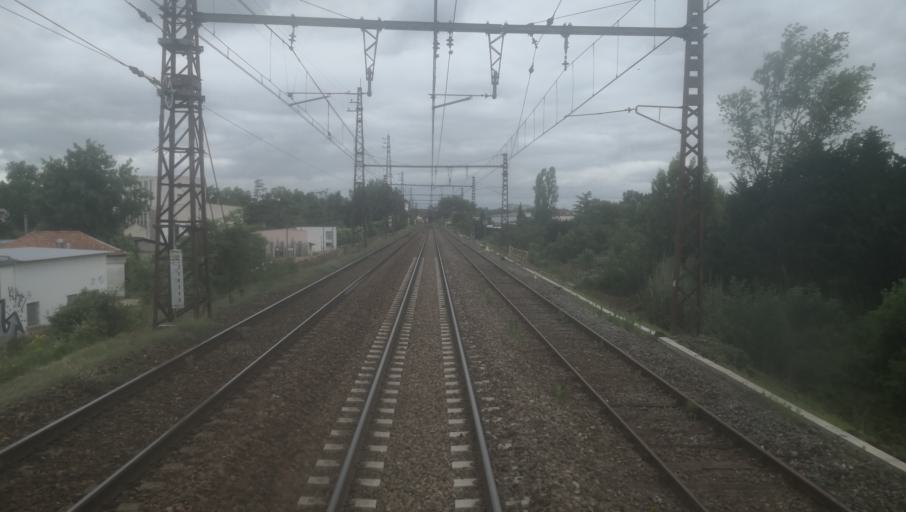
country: FR
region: Midi-Pyrenees
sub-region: Departement du Tarn-et-Garonne
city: Montauban
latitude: 44.0015
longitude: 1.3375
